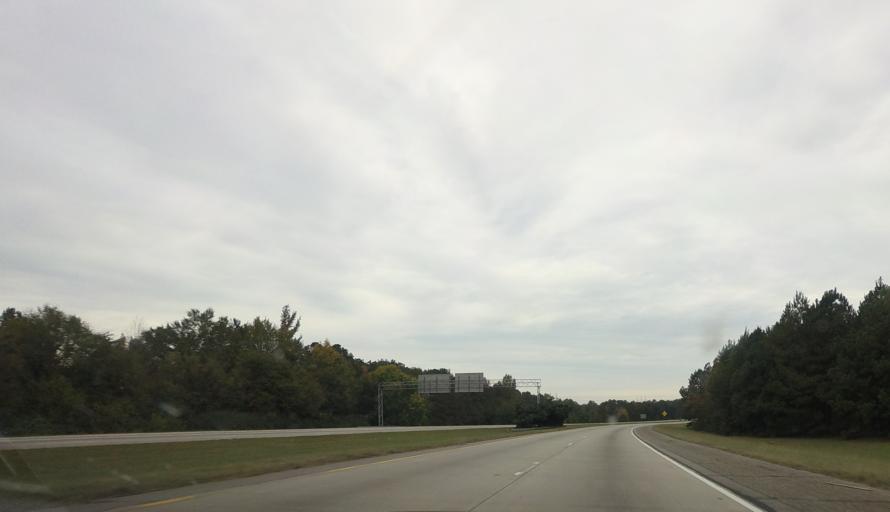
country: US
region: Alabama
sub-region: Russell County
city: Phenix City
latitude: 32.5287
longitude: -84.9759
